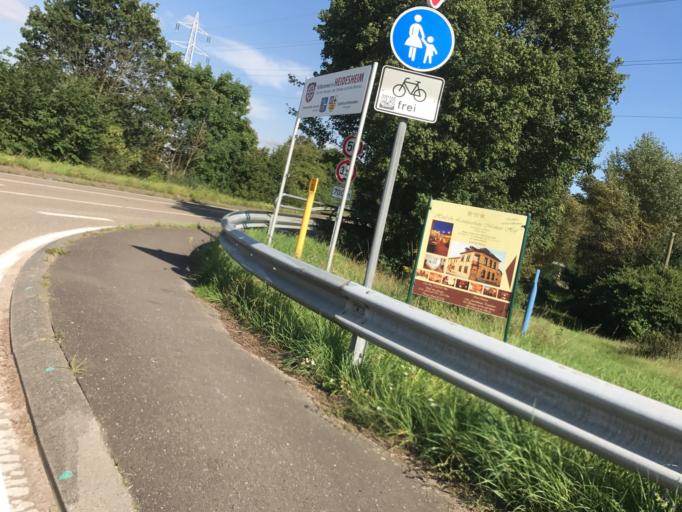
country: DE
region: Rheinland-Pfalz
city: Wackernheim
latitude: 50.0013
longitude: 8.1034
